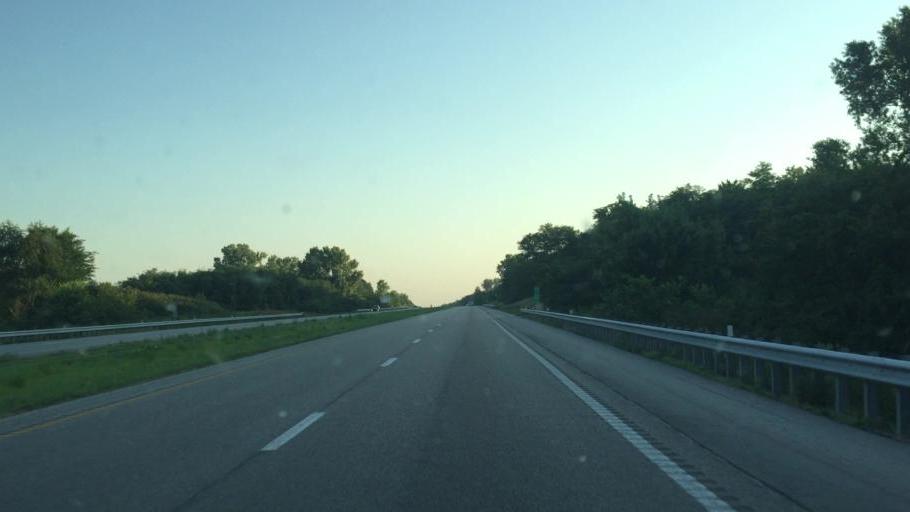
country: US
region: Missouri
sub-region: Platte County
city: Platte City
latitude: 39.4902
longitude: -94.7864
